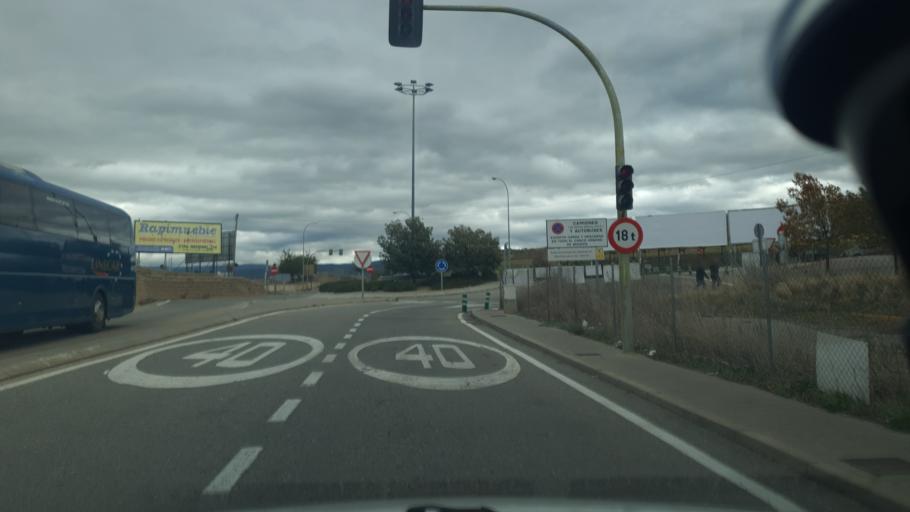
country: ES
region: Castille and Leon
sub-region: Provincia de Segovia
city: Segovia
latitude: 40.9444
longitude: -4.1278
